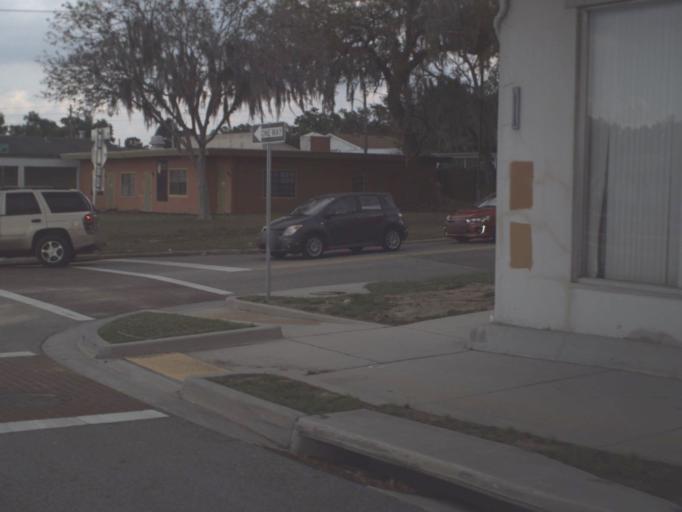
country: US
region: Florida
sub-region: Lake County
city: Eustis
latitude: 28.8544
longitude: -81.6836
